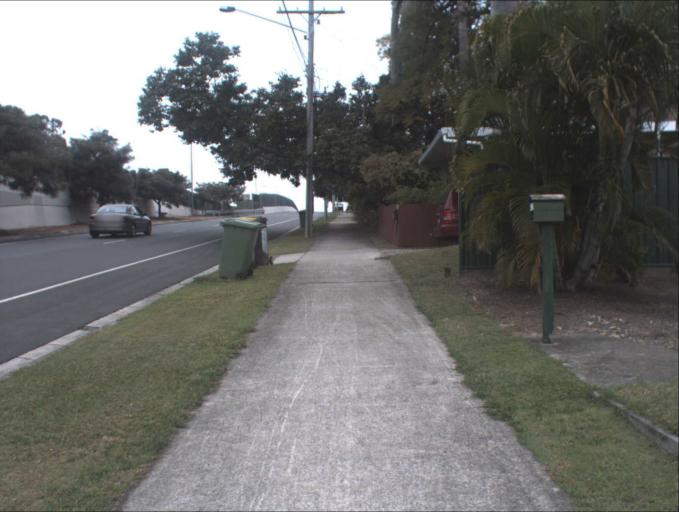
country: AU
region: Queensland
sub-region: Logan
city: Park Ridge South
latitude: -27.6832
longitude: 153.0311
